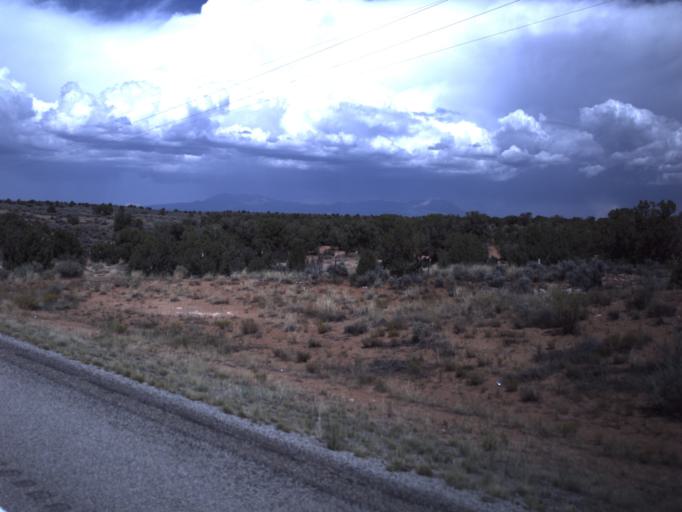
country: US
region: Utah
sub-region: San Juan County
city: Blanding
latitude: 37.4878
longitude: -109.4765
